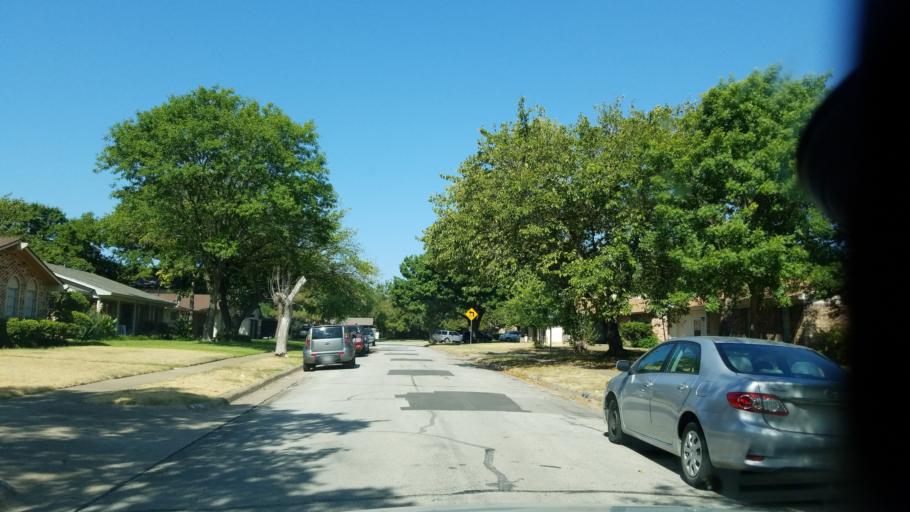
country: US
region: Texas
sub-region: Dallas County
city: Duncanville
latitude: 32.6397
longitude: -96.9019
